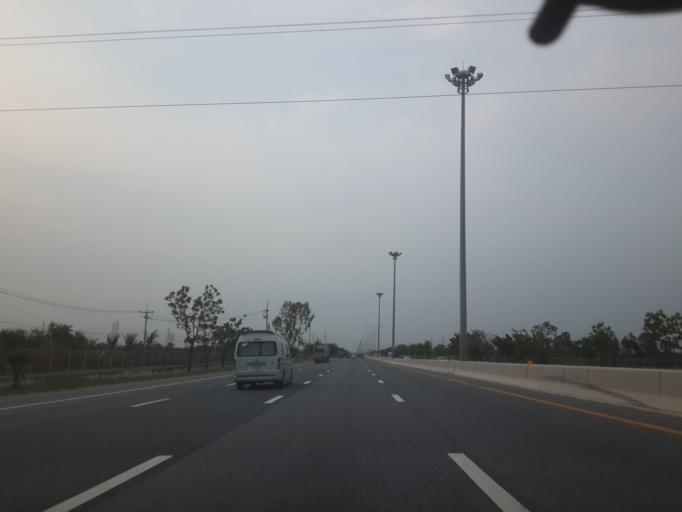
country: TH
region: Chachoengsao
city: Bang Pakong
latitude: 13.5121
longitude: 101.0317
